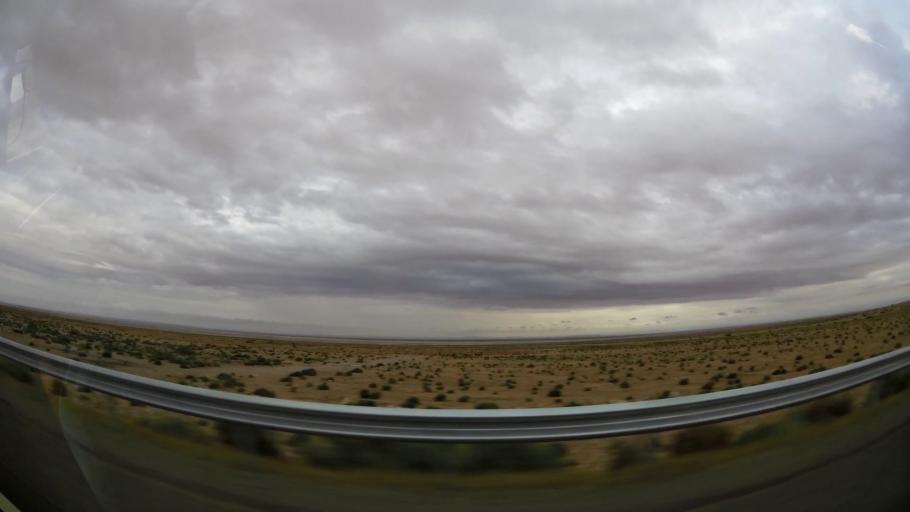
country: MA
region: Taza-Al Hoceima-Taounate
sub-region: Taza
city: Guercif
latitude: 34.3058
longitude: -3.6218
